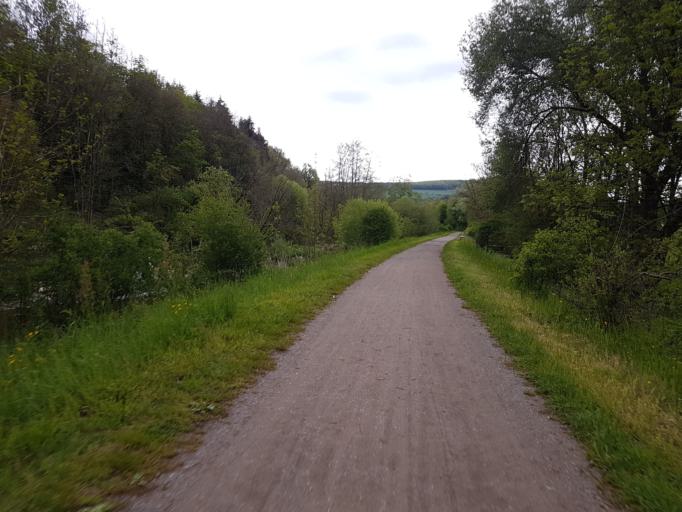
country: DE
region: Baden-Wuerttemberg
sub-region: Freiburg Region
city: Lauchringen
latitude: 47.6245
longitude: 8.3003
